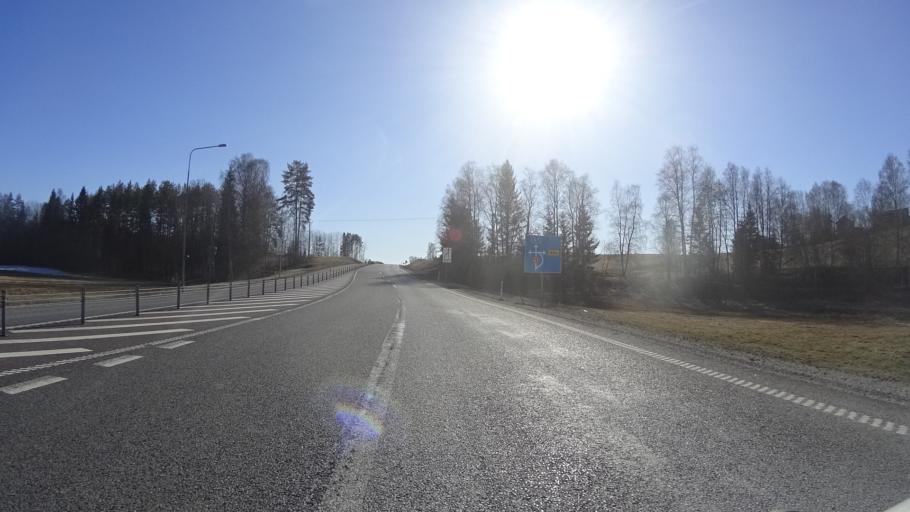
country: SE
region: Vaermland
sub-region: Arvika Kommun
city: Arvika
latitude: 59.6672
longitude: 12.7965
